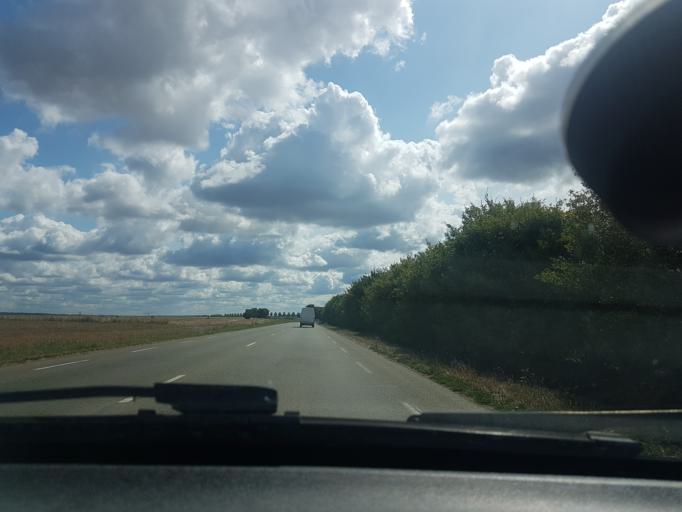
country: FR
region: Ile-de-France
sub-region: Departement des Yvelines
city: Plaisir
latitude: 48.8362
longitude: 1.9522
